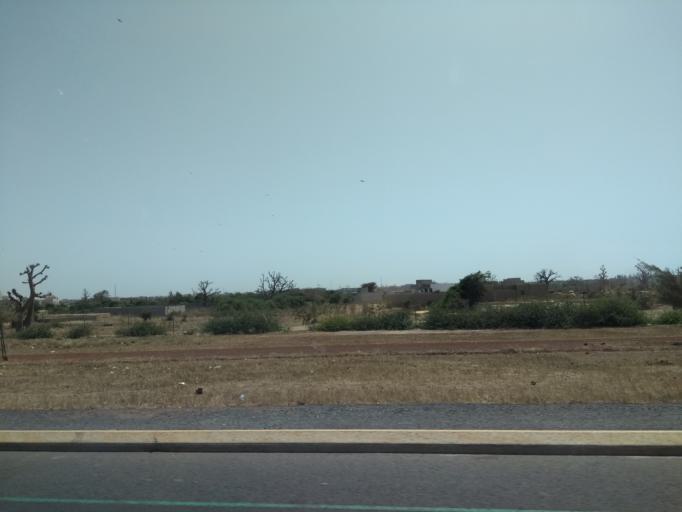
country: SN
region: Thies
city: Thies
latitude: 14.7377
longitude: -17.1813
